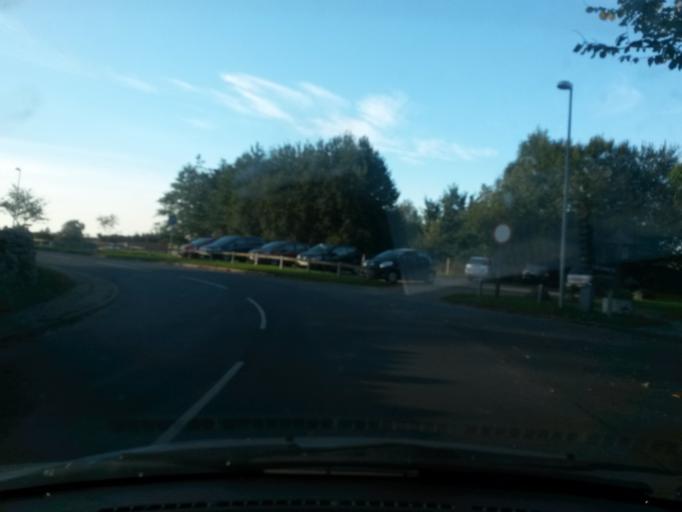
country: DK
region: Central Jutland
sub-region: Silkeborg Kommune
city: Kjellerup
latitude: 56.3293
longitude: 9.4426
